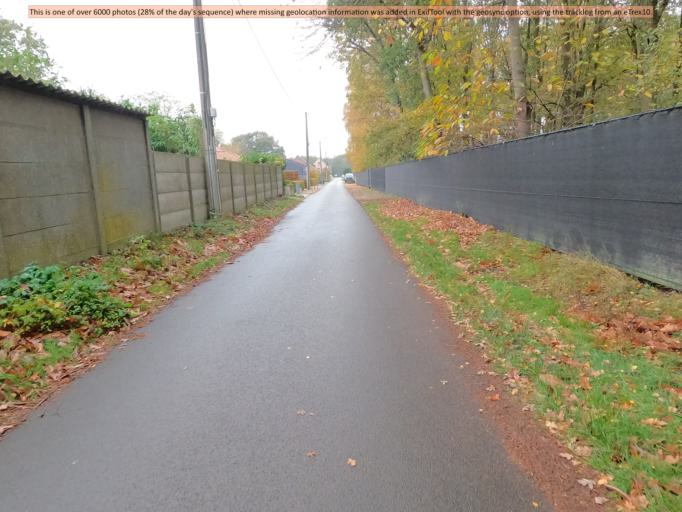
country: BE
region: Flanders
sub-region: Provincie Antwerpen
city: Nijlen
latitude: 51.1600
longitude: 4.6531
